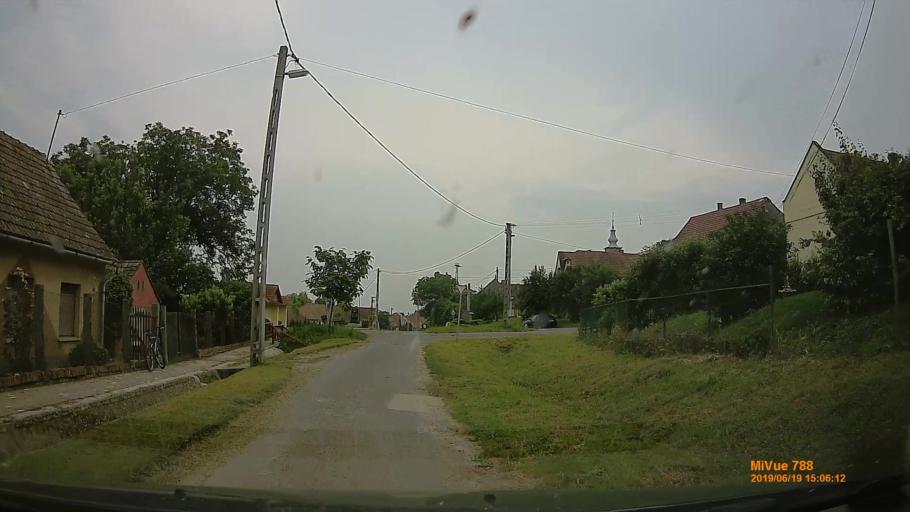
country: HU
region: Baranya
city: Szigetvar
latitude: 46.0984
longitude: 17.8067
